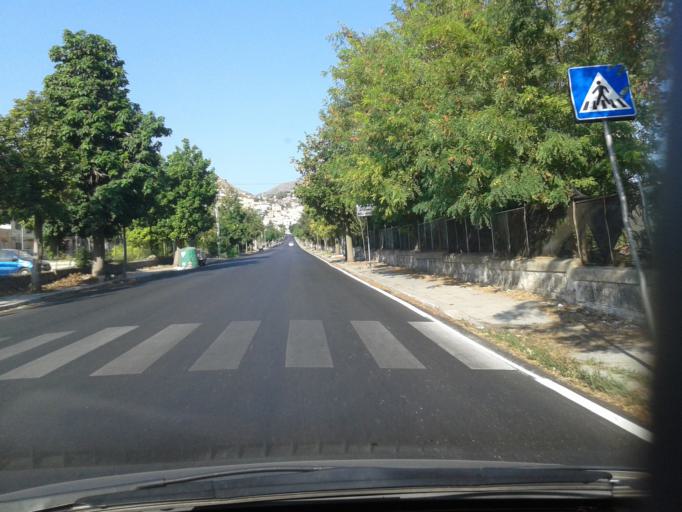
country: IT
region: Sicily
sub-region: Palermo
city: Palermo
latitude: 38.1100
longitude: 13.3177
